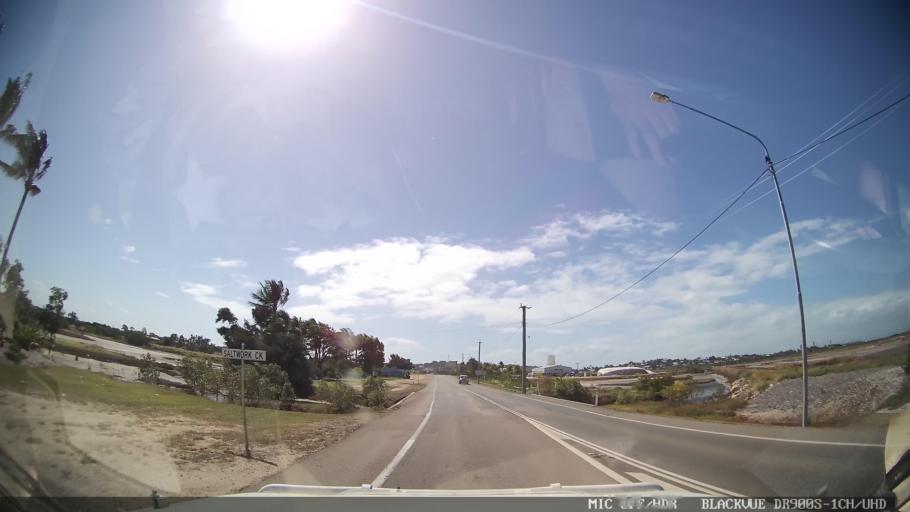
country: AU
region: Queensland
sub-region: Whitsunday
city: Bowen
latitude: -20.0143
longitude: 148.2226
